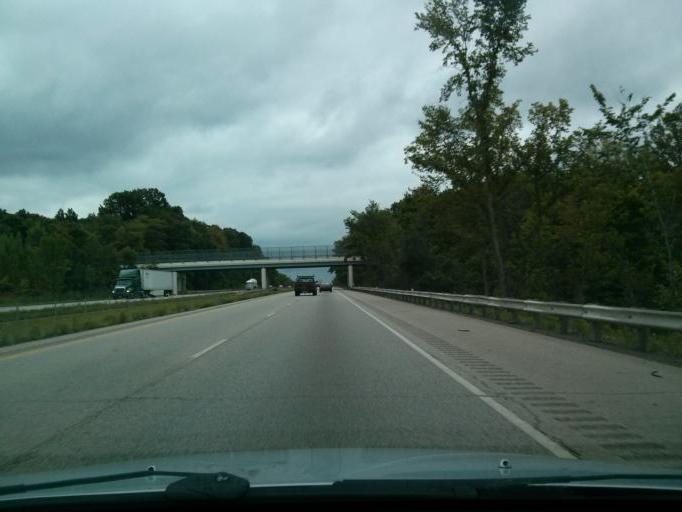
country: US
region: Ohio
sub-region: Mahoning County
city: Craig Beach
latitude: 41.1059
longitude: -81.0912
